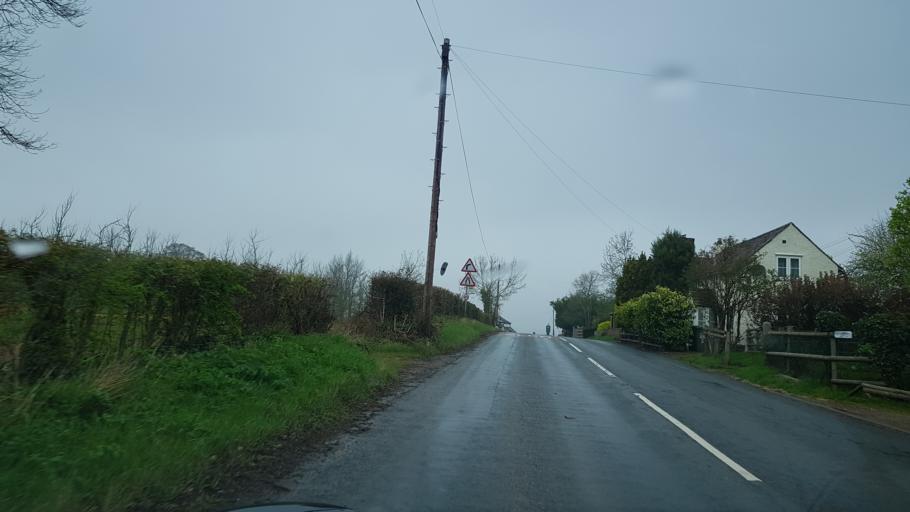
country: GB
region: England
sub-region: Herefordshire
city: Ledbury
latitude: 52.0698
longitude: -2.4513
